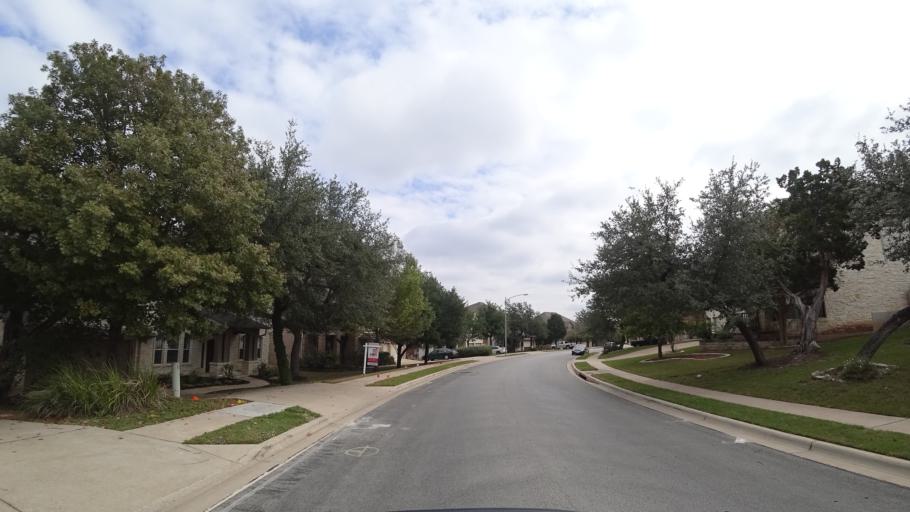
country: US
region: Texas
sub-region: Travis County
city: Shady Hollow
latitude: 30.2184
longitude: -97.8864
